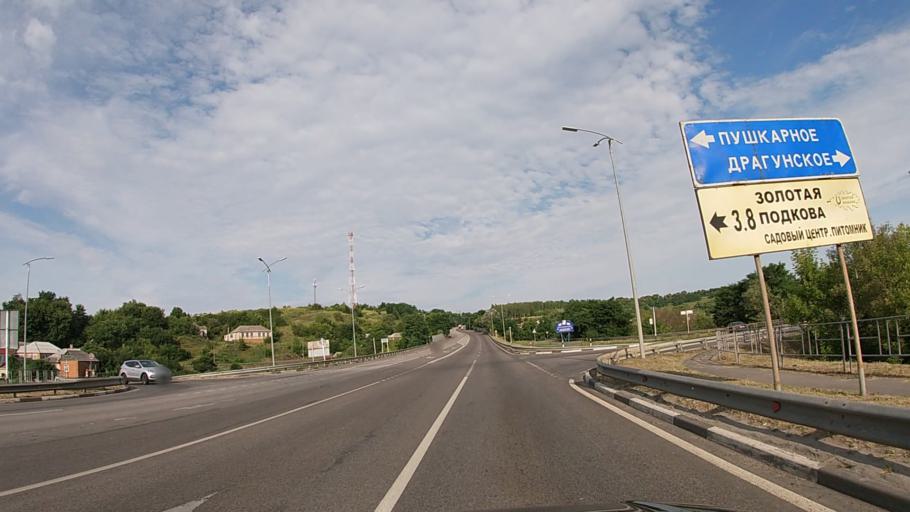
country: RU
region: Belgorod
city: Severnyy
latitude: 50.6357
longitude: 36.4622
